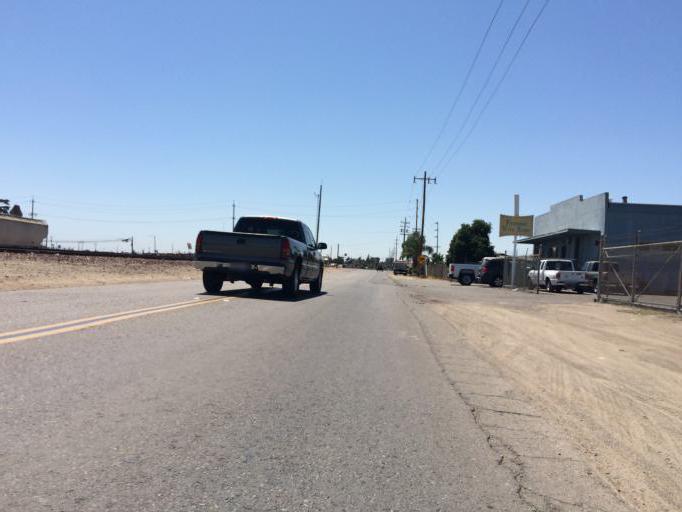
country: US
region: California
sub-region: Fresno County
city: Fresno
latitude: 36.7159
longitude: -119.7727
